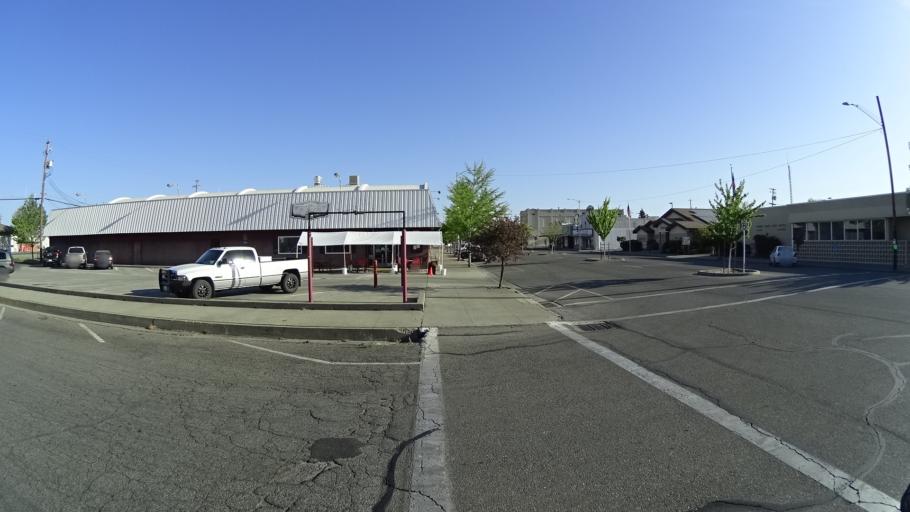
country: US
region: California
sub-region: Glenn County
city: Orland
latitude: 39.7451
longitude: -122.1943
